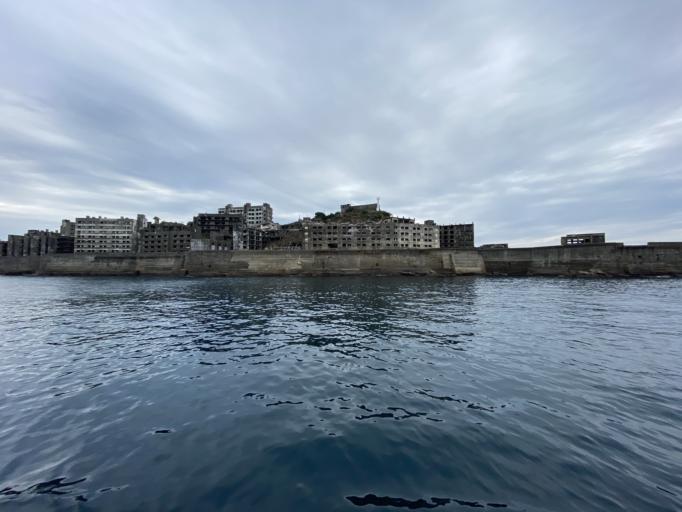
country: JP
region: Nagasaki
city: Nagasaki-shi
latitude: 32.6277
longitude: 129.7360
